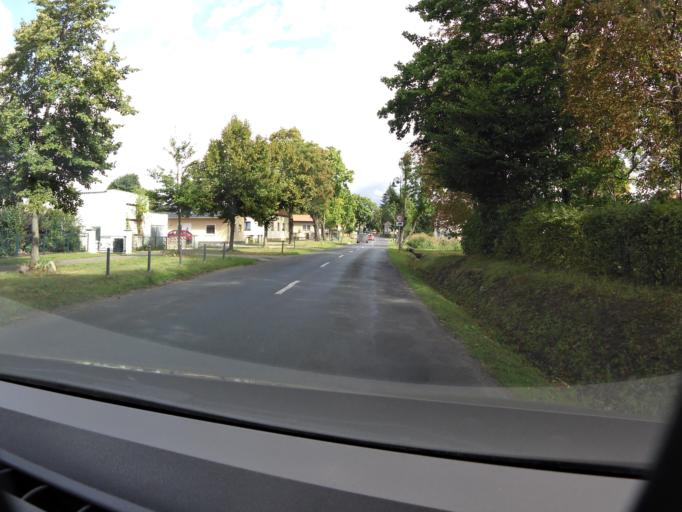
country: DE
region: Brandenburg
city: Rauen
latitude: 52.3320
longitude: 14.0271
